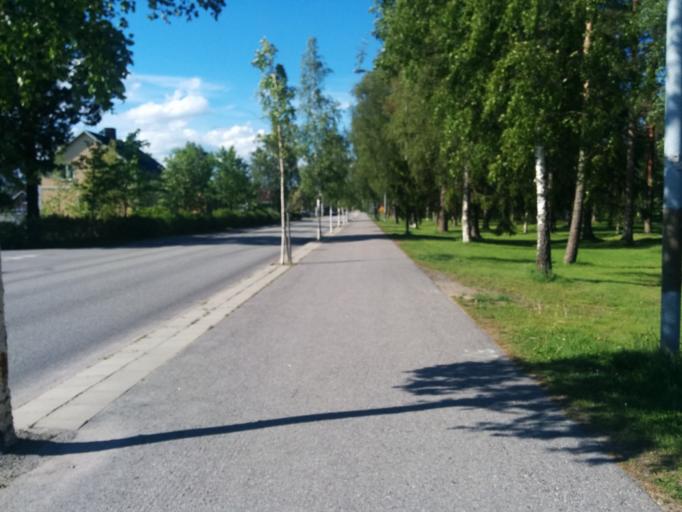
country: SE
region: Vaesterbotten
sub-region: Umea Kommun
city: Hoernefors
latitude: 63.6248
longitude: 19.9086
